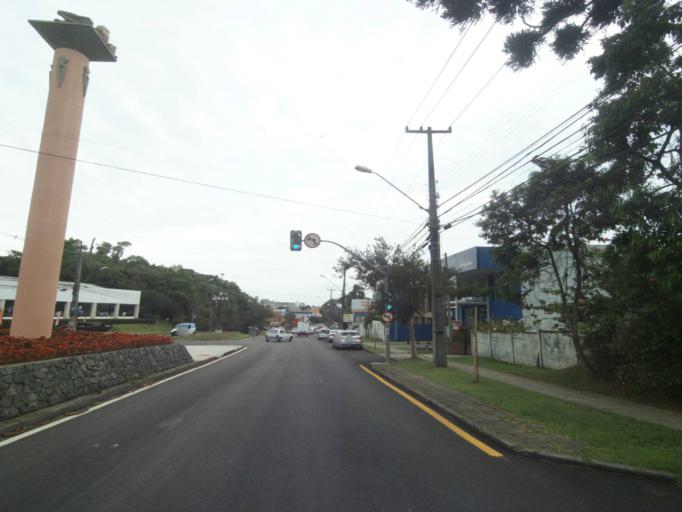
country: BR
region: Parana
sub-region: Curitiba
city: Curitiba
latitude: -25.4178
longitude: -49.2941
